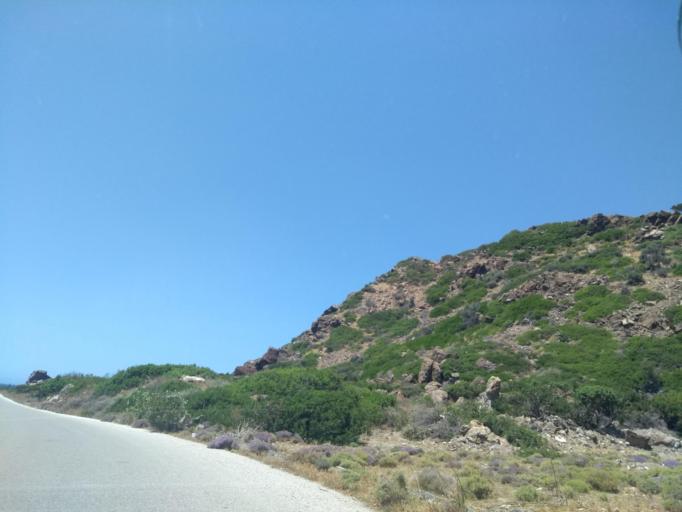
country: GR
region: Crete
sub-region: Nomos Chanias
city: Vryses
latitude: 35.3500
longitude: 23.5383
